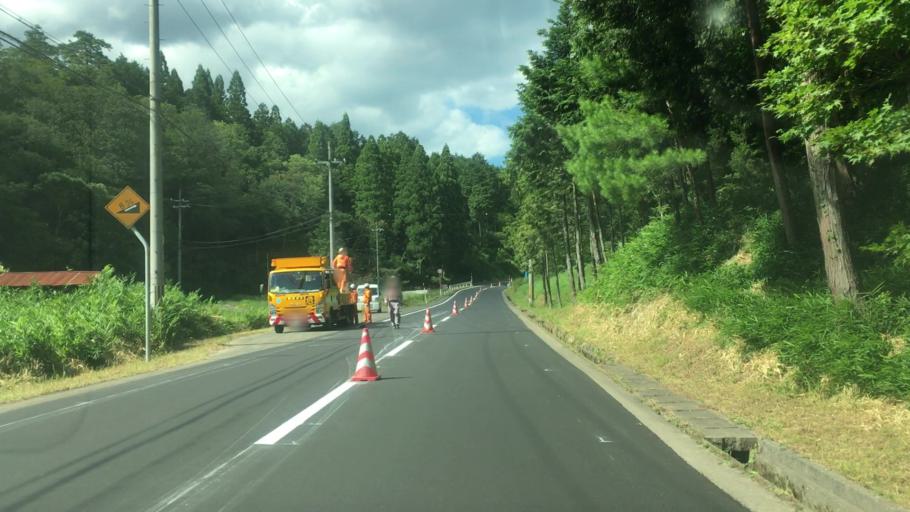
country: JP
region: Hyogo
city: Toyooka
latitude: 35.5056
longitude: 134.7772
